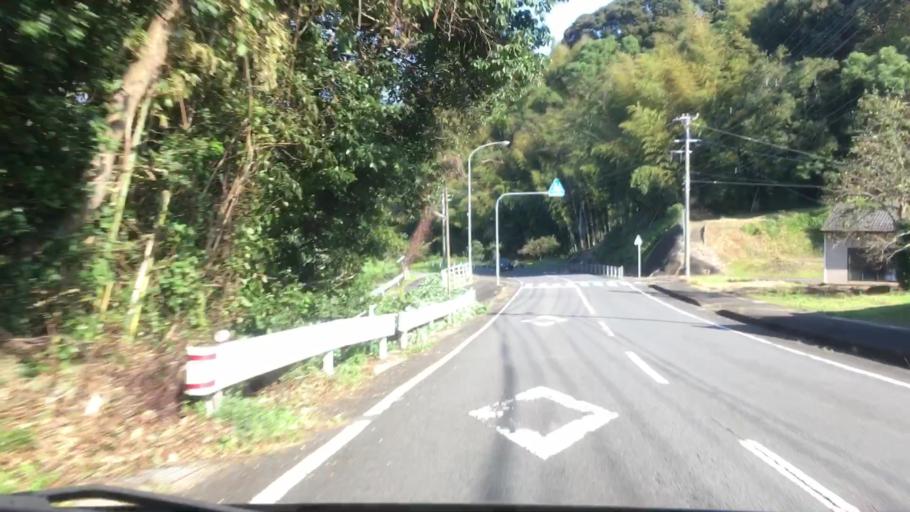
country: JP
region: Nagasaki
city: Sasebo
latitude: 33.0103
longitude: 129.6560
